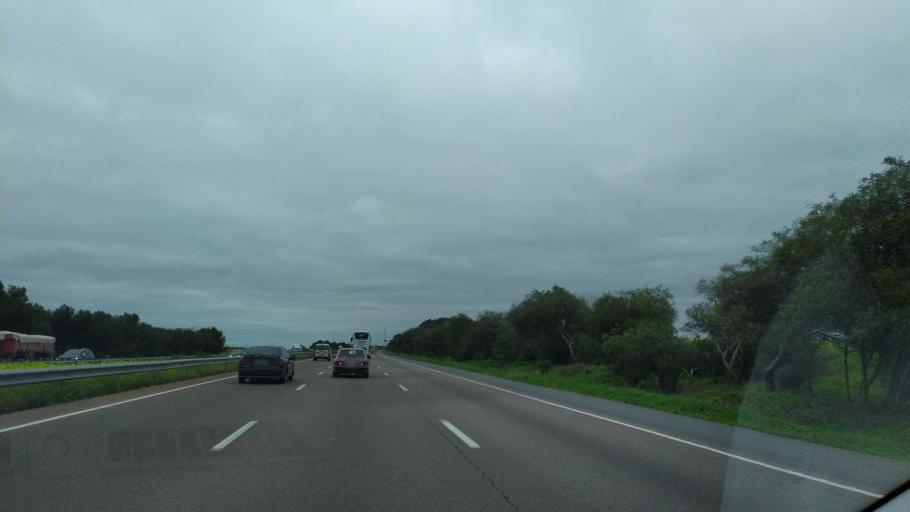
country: MA
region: Chaouia-Ouardigha
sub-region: Benslimane
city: Bouznika
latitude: 33.7541
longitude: -7.2783
